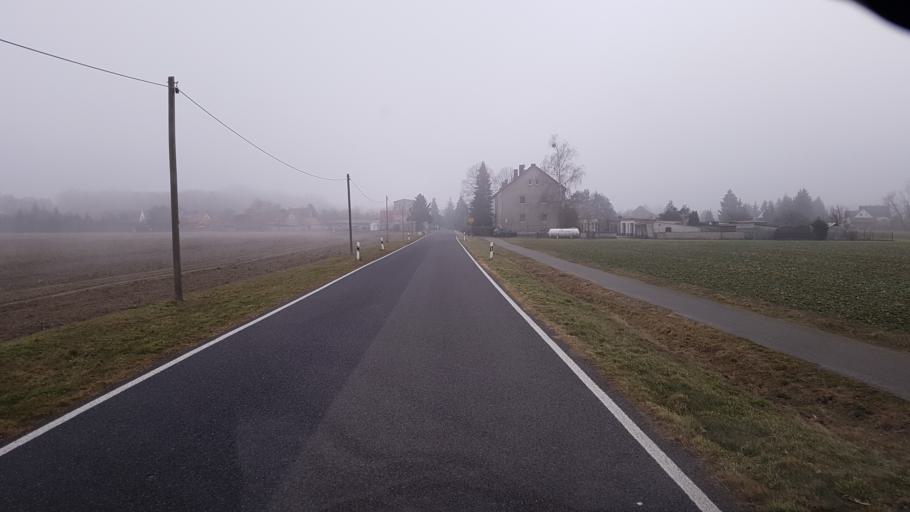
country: DE
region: Saxony-Anhalt
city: Holzdorf
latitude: 51.8454
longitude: 13.2161
